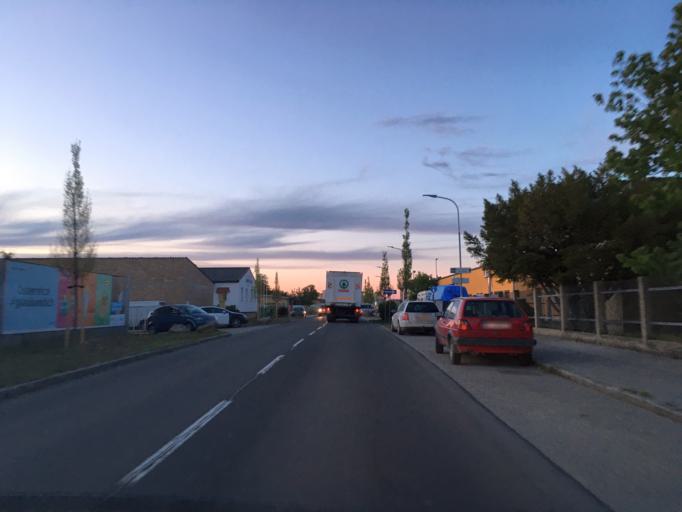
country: AT
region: Lower Austria
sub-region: Politischer Bezirk Wien-Umgebung
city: Zwolfaxing
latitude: 48.1189
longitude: 16.4684
